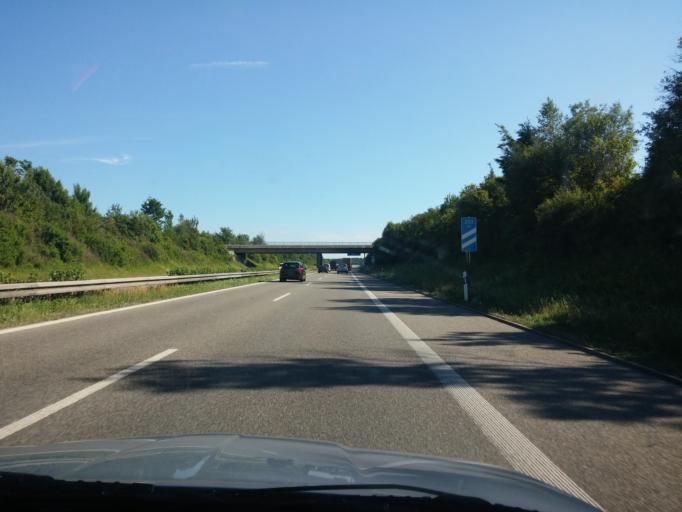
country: DE
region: Baden-Wuerttemberg
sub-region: Tuebingen Region
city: Leutkirch im Allgau
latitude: 47.8192
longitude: 9.9912
